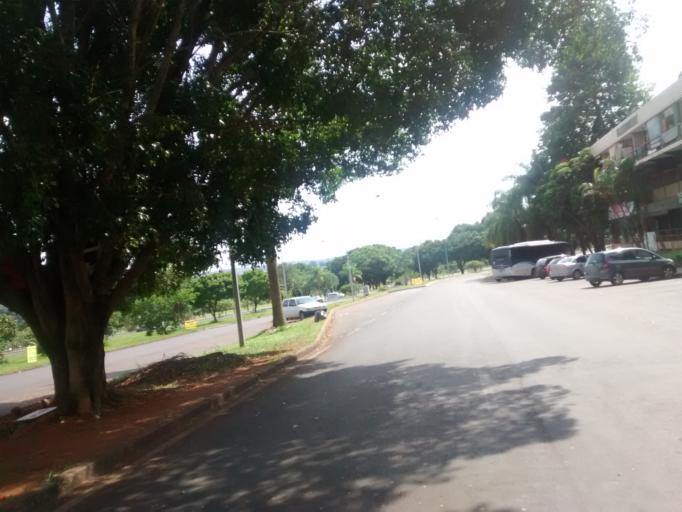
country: BR
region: Federal District
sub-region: Brasilia
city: Brasilia
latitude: -15.7370
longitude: -47.8943
